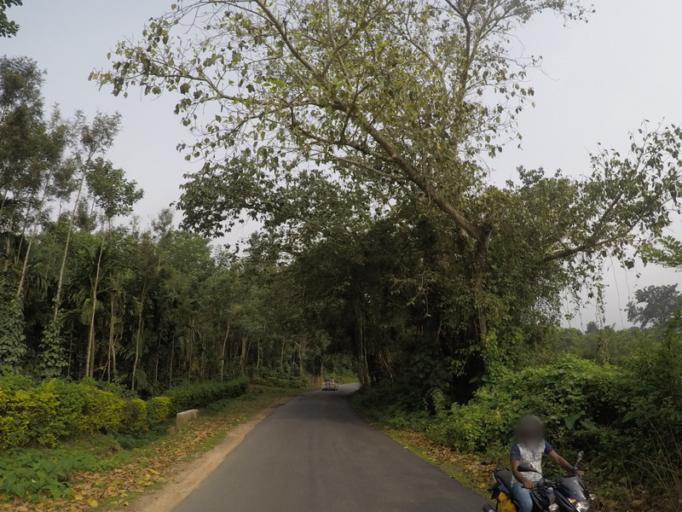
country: IN
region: Karnataka
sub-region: Chikmagalur
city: Chikmagalur
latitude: 13.3421
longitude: 75.5440
